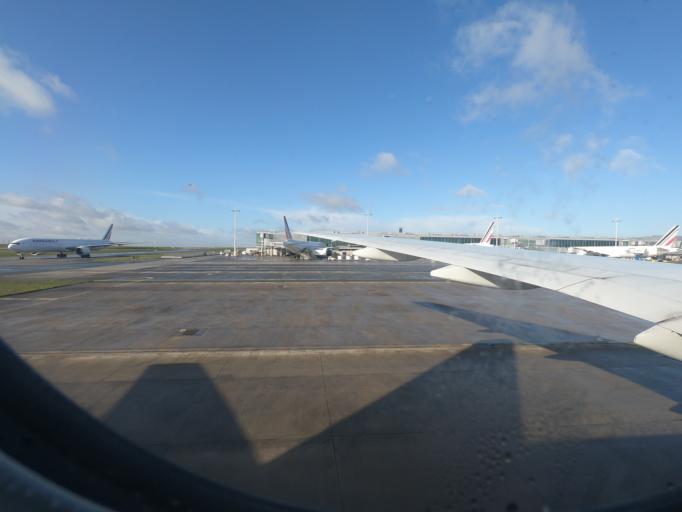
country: FR
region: Ile-de-France
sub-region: Departement de Seine-et-Marne
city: Mitry-Mory
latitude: 49.0015
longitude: 2.5888
